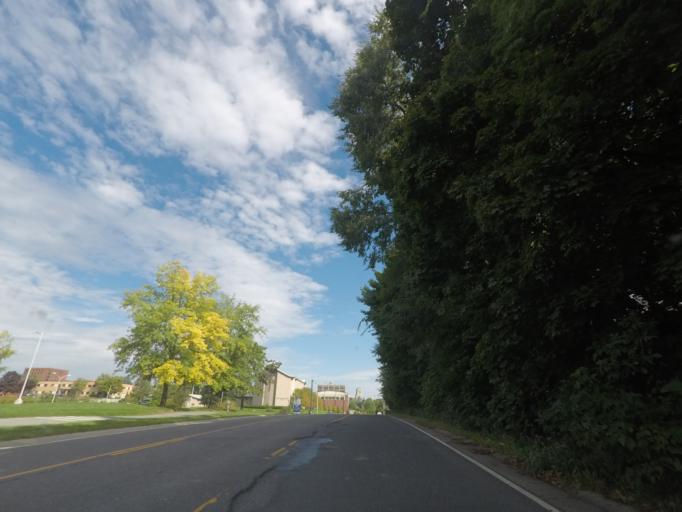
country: US
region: New York
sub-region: Albany County
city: Albany
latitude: 42.6449
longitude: -73.7795
